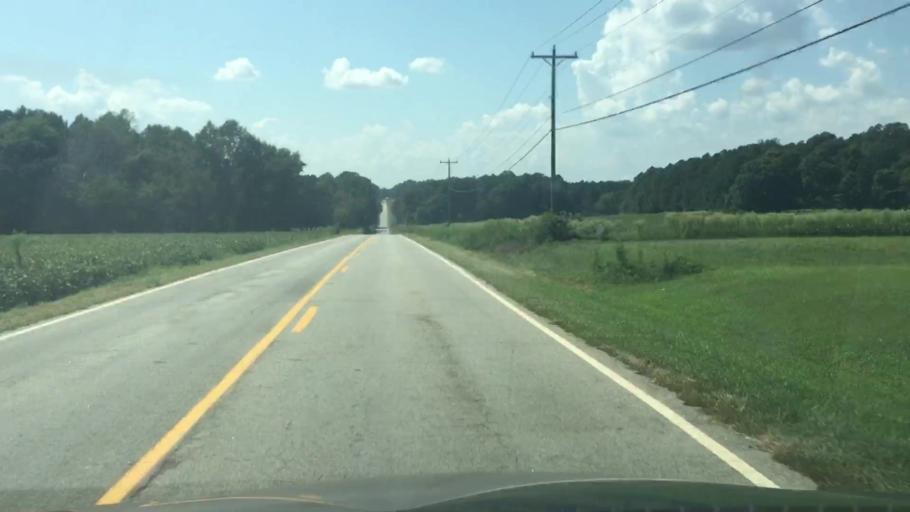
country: US
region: North Carolina
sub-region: Rowan County
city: China Grove
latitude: 35.6495
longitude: -80.6094
